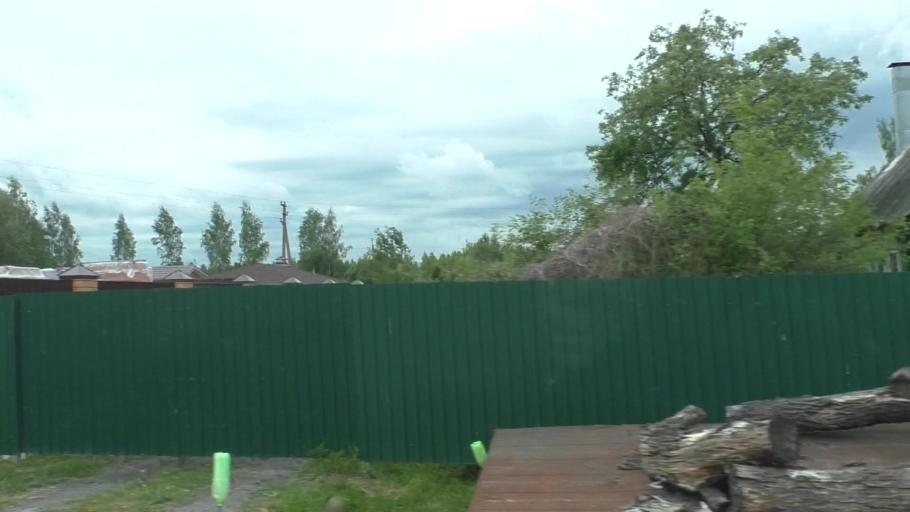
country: RU
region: Moskovskaya
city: Il'inskiy Pogost
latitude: 55.4691
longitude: 38.8972
